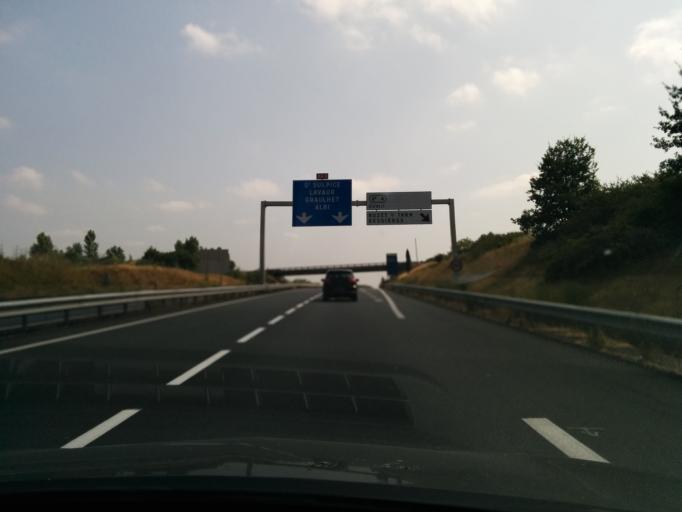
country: FR
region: Midi-Pyrenees
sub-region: Departement de la Haute-Garonne
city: Montastruc-la-Conseillere
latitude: 43.7392
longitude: 1.5888
